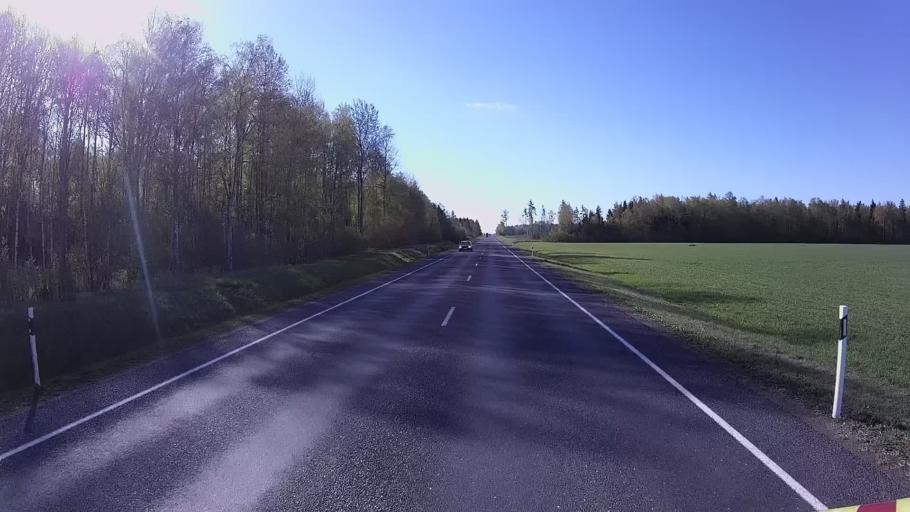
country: EE
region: Viljandimaa
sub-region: Vohma linn
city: Vohma
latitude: 58.7222
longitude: 25.6040
